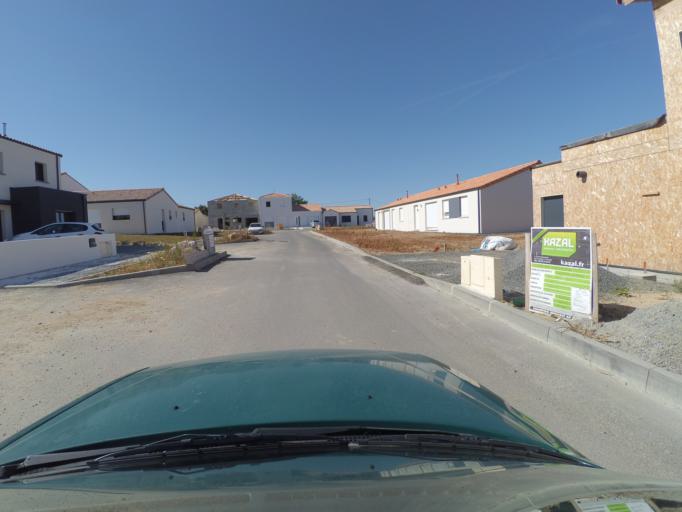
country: FR
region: Pays de la Loire
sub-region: Departement de la Loire-Atlantique
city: Aigrefeuille-sur-Maine
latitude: 47.0863
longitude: -1.4094
